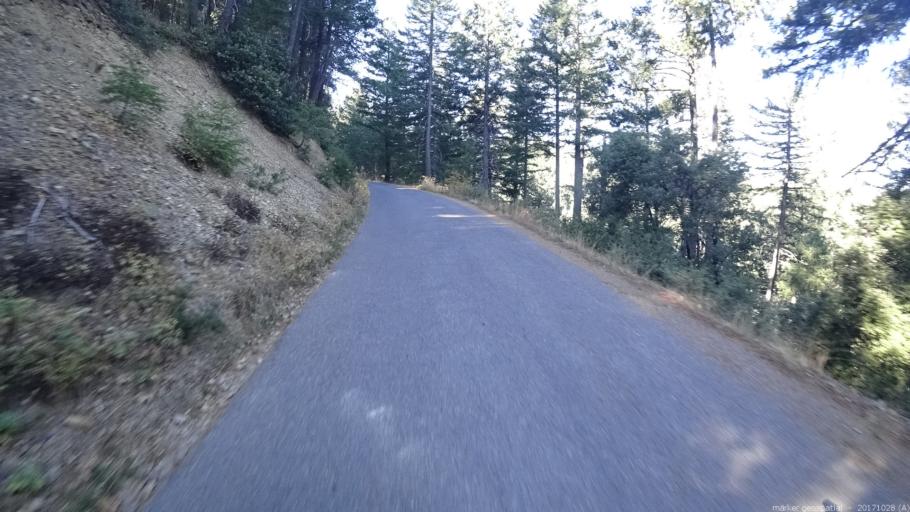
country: US
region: California
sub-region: Trinity County
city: Lewiston
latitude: 40.8220
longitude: -122.6566
